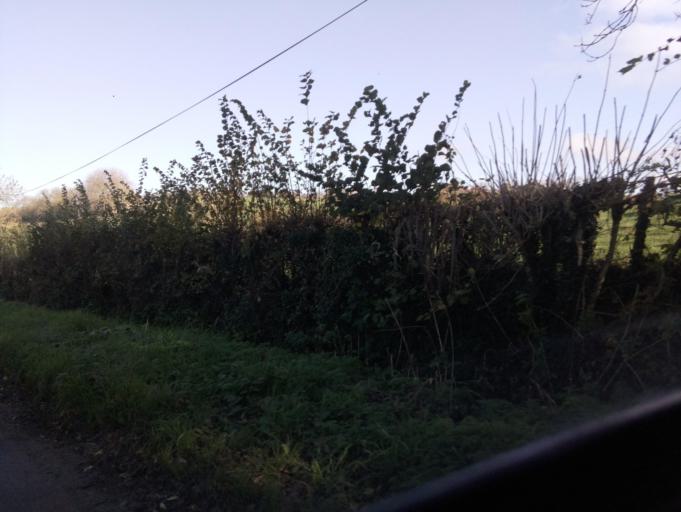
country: GB
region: England
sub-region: Somerset
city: Castle Cary
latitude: 51.0608
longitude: -2.4783
